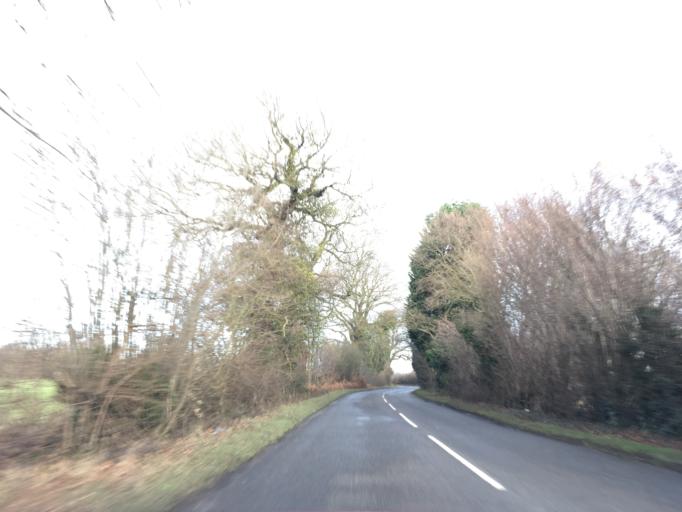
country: GB
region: England
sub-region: Nottinghamshire
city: South Collingham
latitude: 53.1844
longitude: -0.7463
